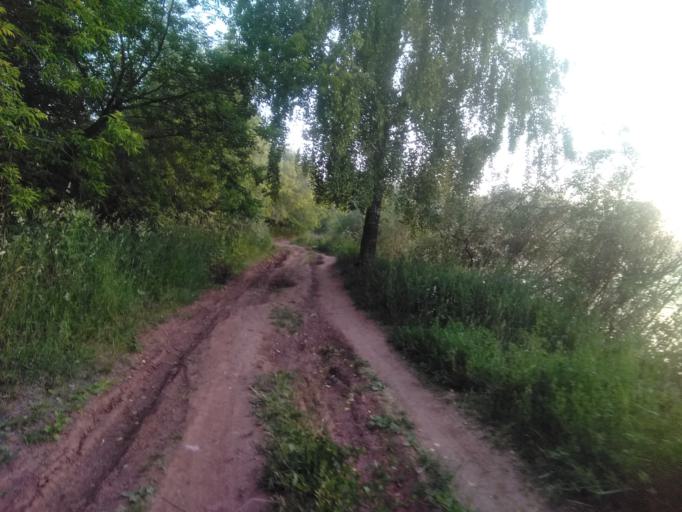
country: RU
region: Udmurtiya
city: Khokhryaki
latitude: 56.8545
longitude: 53.4055
